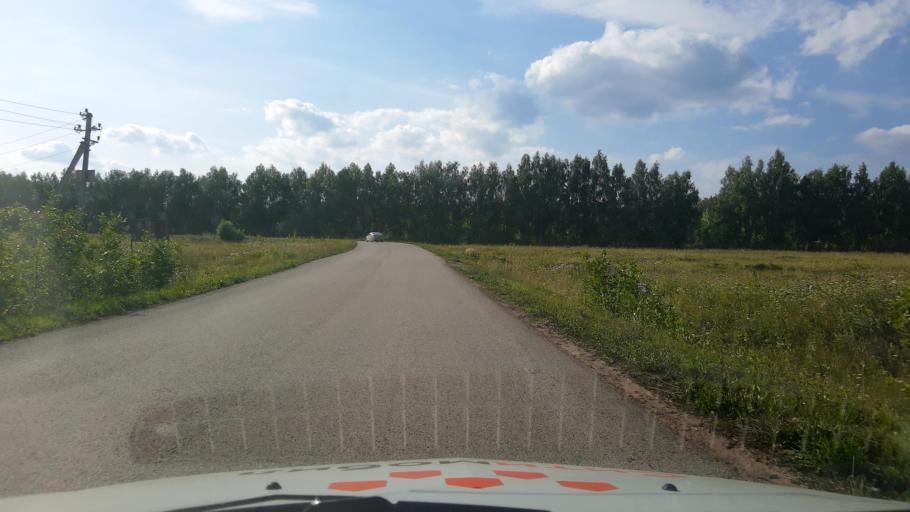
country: RU
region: Bashkortostan
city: Kabakovo
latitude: 54.6625
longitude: 56.1968
